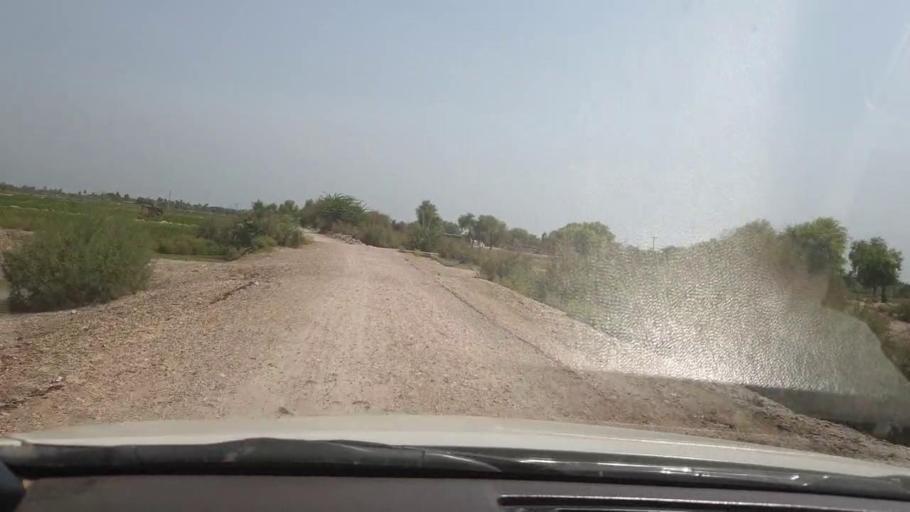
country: PK
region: Sindh
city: Shikarpur
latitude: 27.9268
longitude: 68.6049
